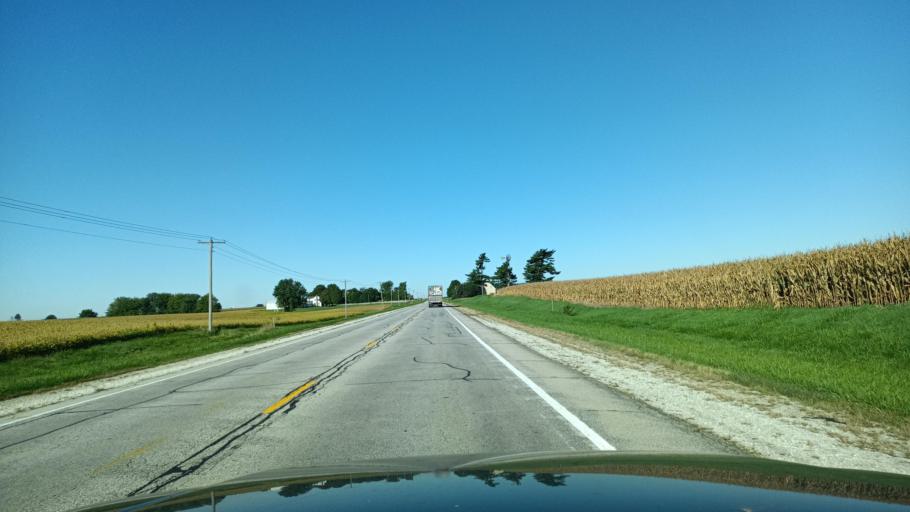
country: US
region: Illinois
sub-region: Warren County
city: Monmouth
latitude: 40.8785
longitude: -90.7058
